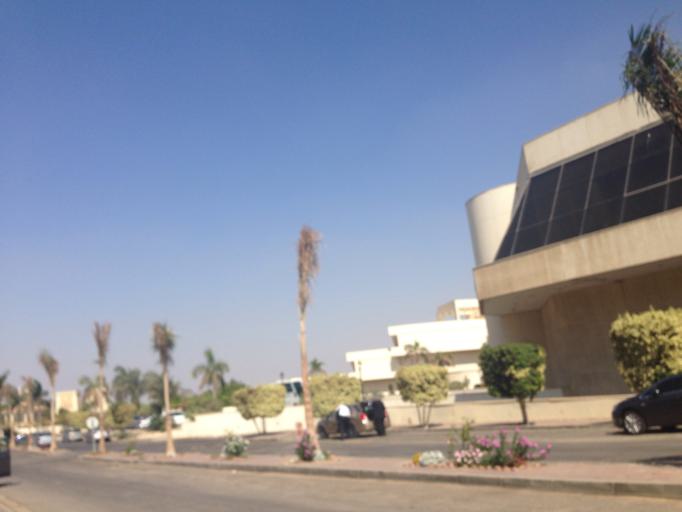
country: EG
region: Muhafazat al Qalyubiyah
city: Al Khankah
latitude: 30.0712
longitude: 31.4337
